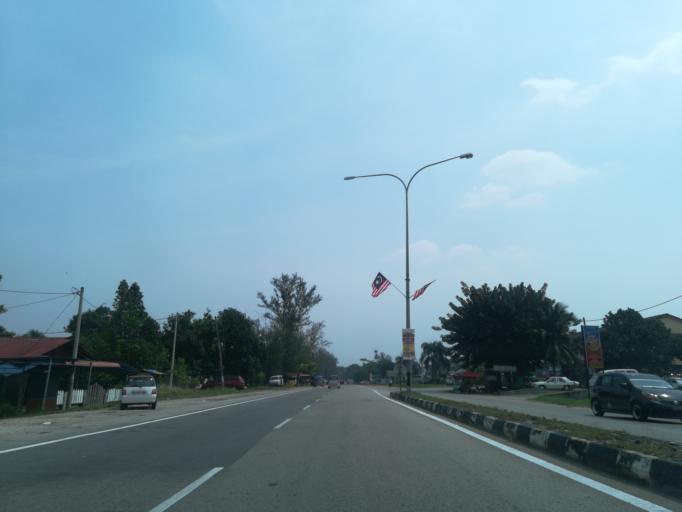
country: MY
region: Kedah
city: Kulim
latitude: 5.4215
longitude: 100.5375
